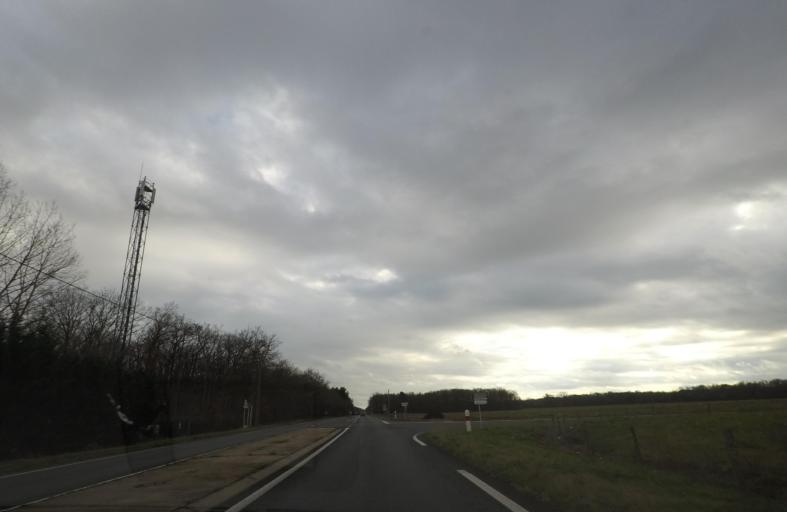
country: FR
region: Centre
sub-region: Departement du Loir-et-Cher
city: Soings-en-Sologne
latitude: 47.4316
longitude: 1.5638
